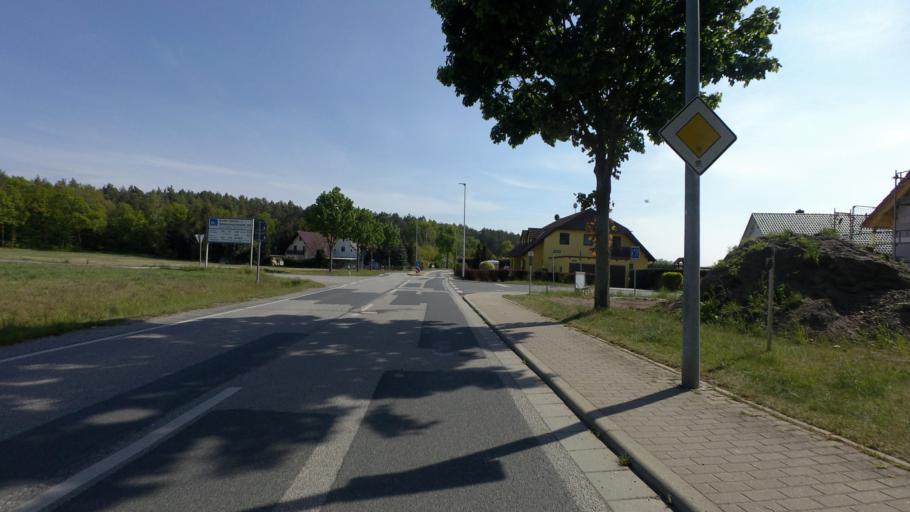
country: DE
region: Saxony
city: Ossling
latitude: 51.3574
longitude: 14.1665
